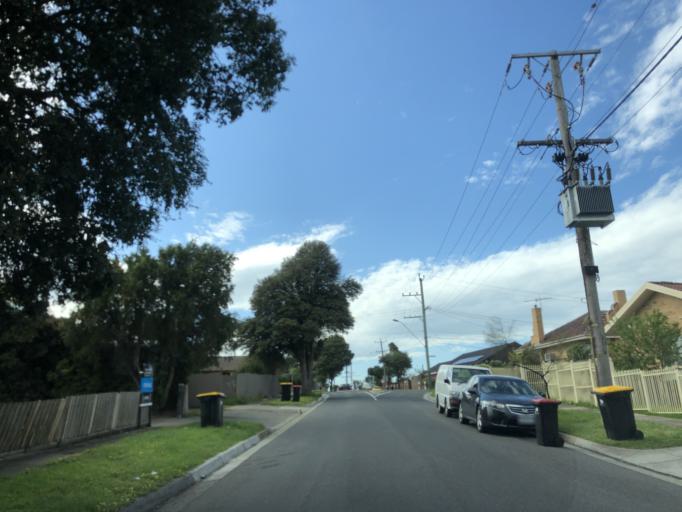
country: AU
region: Victoria
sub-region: Greater Dandenong
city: Dandenong
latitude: -37.9764
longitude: 145.2012
